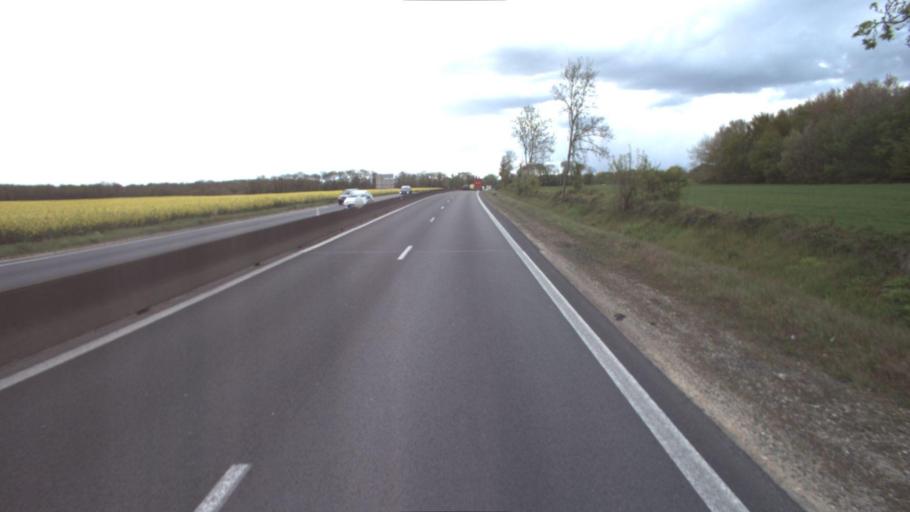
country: FR
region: Ile-de-France
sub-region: Departement de Seine-et-Marne
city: Tournan-en-Brie
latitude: 48.7360
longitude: 2.7545
